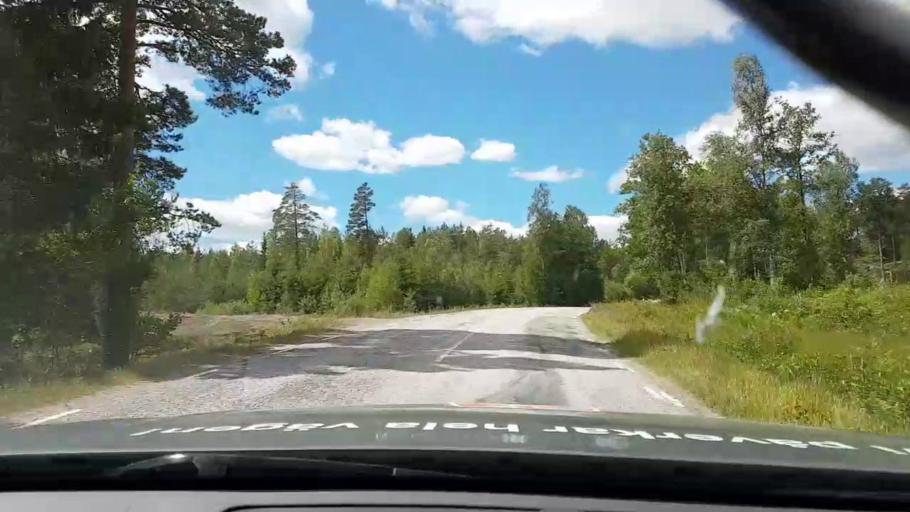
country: SE
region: Kalmar
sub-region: Vasterviks Kommun
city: Forserum
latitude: 58.0253
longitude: 16.5460
